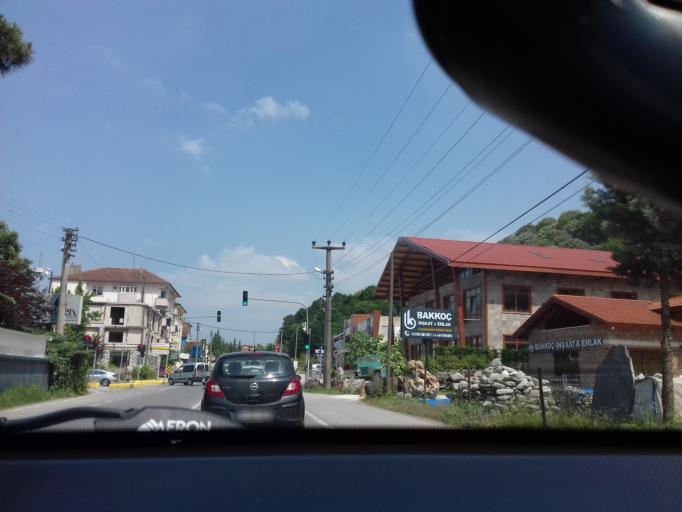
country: TR
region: Sakarya
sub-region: Merkez
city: Sapanca
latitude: 40.6908
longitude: 30.2226
